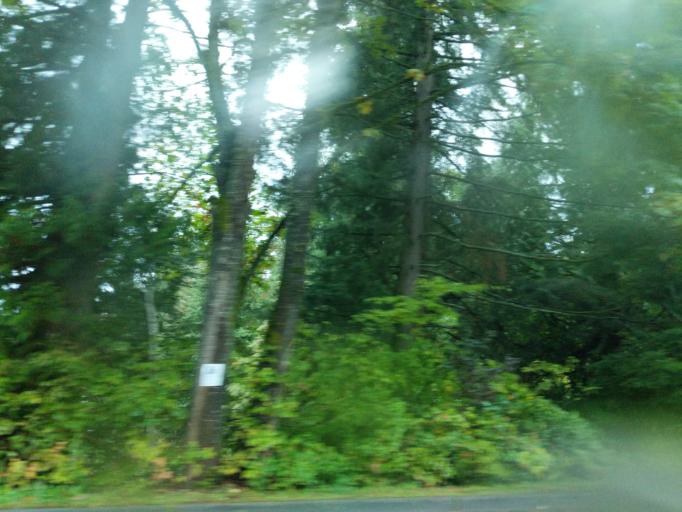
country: US
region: Washington
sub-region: King County
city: Bothell
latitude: 47.7701
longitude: -122.2070
